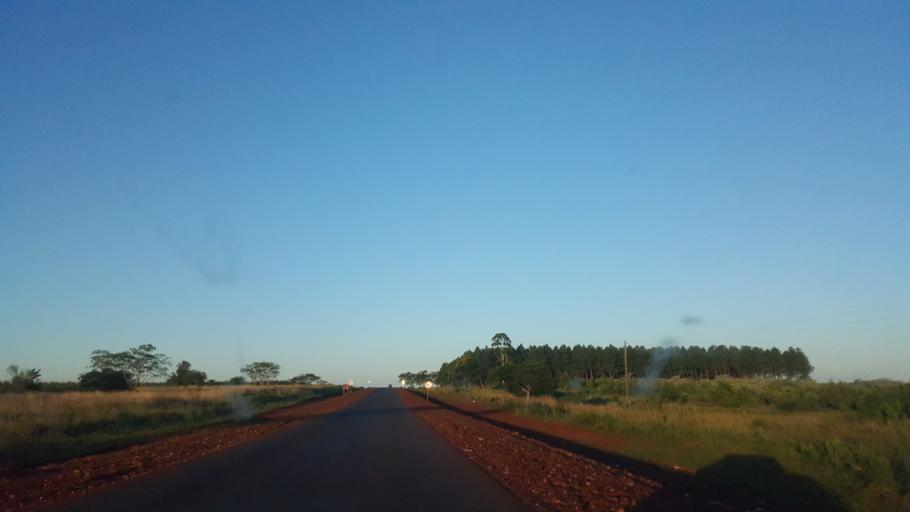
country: AR
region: Corrientes
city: Santo Tome
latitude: -28.5026
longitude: -56.0551
